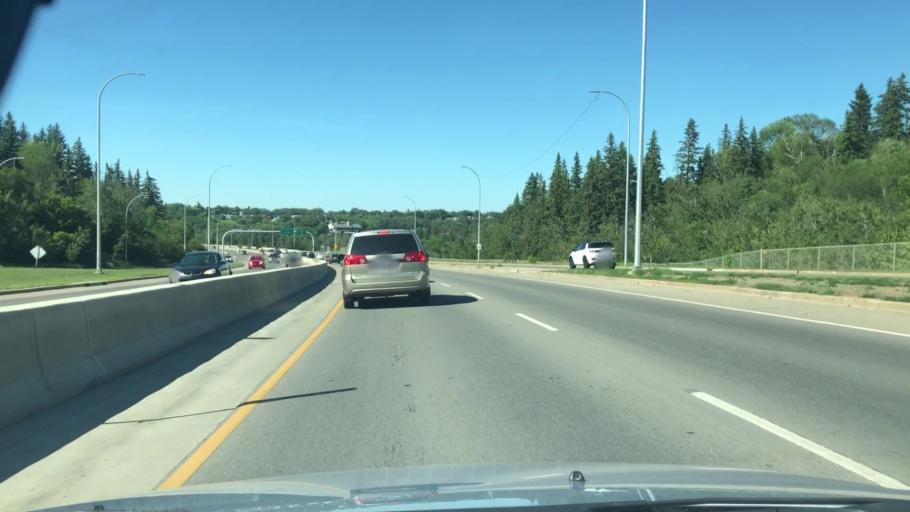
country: CA
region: Alberta
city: Edmonton
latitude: 53.5515
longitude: -113.4379
